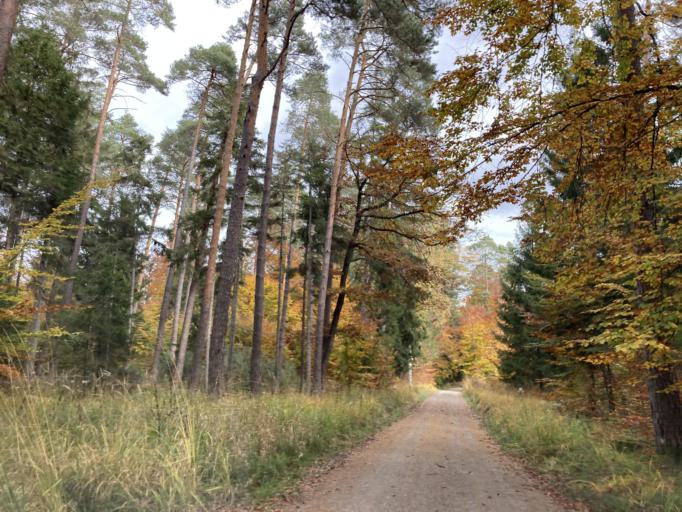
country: DE
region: Baden-Wuerttemberg
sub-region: Tuebingen Region
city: Bodelshausen
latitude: 48.4435
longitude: 8.9842
